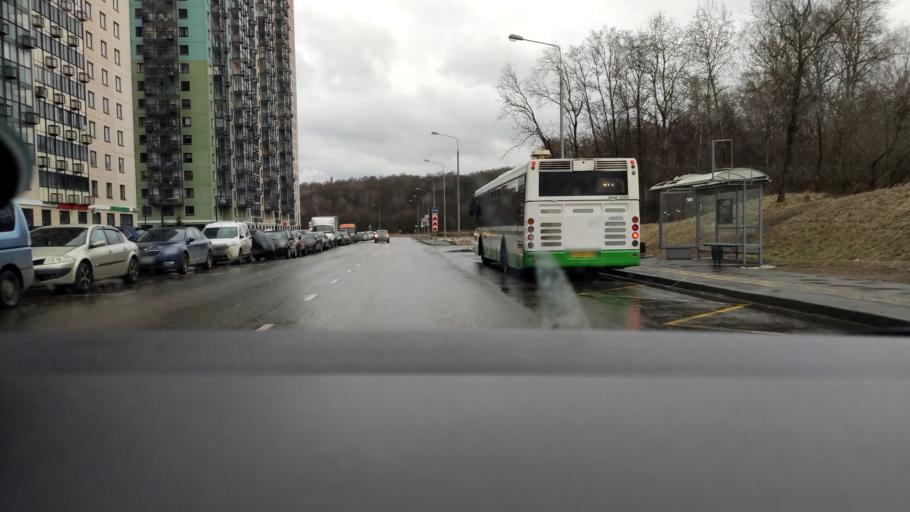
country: RU
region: Moskovskaya
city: Pavshino
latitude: 55.8614
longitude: 37.3719
